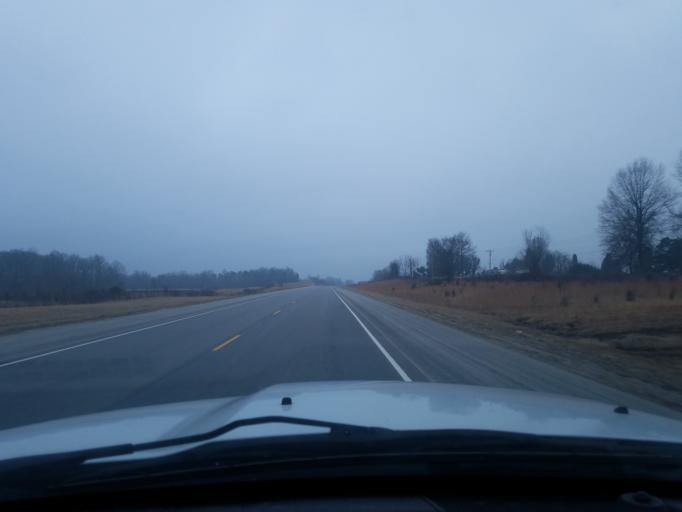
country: US
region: Indiana
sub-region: Crawford County
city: English
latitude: 38.2139
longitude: -86.5932
